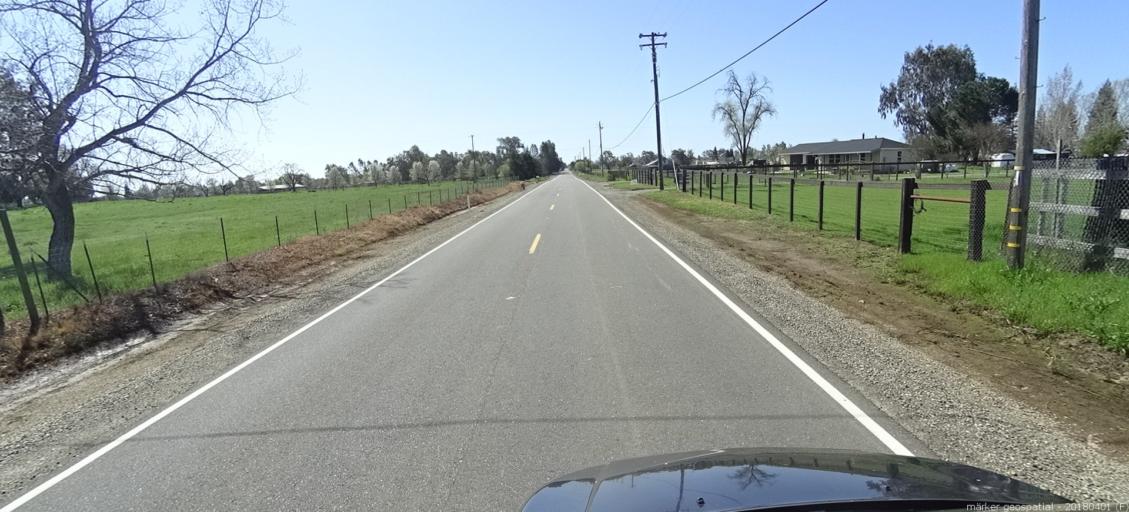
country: US
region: California
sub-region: Sacramento County
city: Wilton
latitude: 38.4051
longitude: -121.2240
